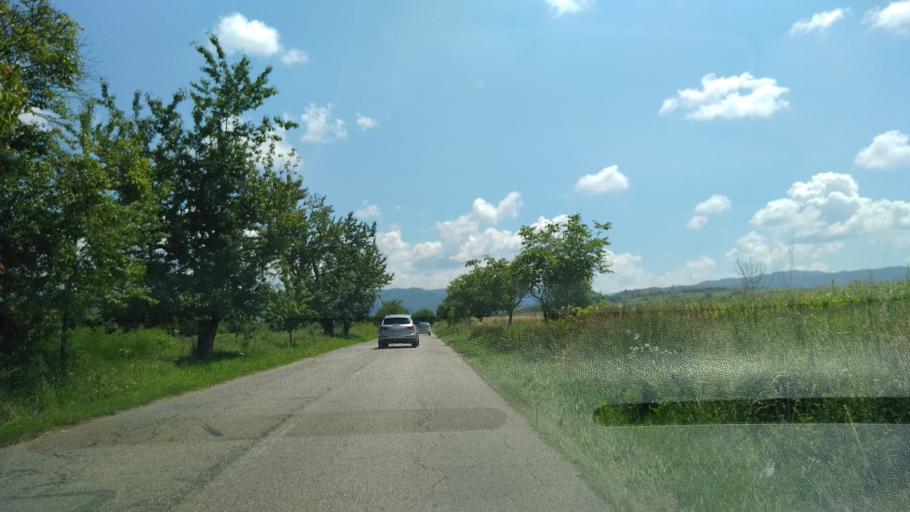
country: RO
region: Hunedoara
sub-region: Comuna Bosorod
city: Bosorod
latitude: 45.7115
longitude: 23.0447
